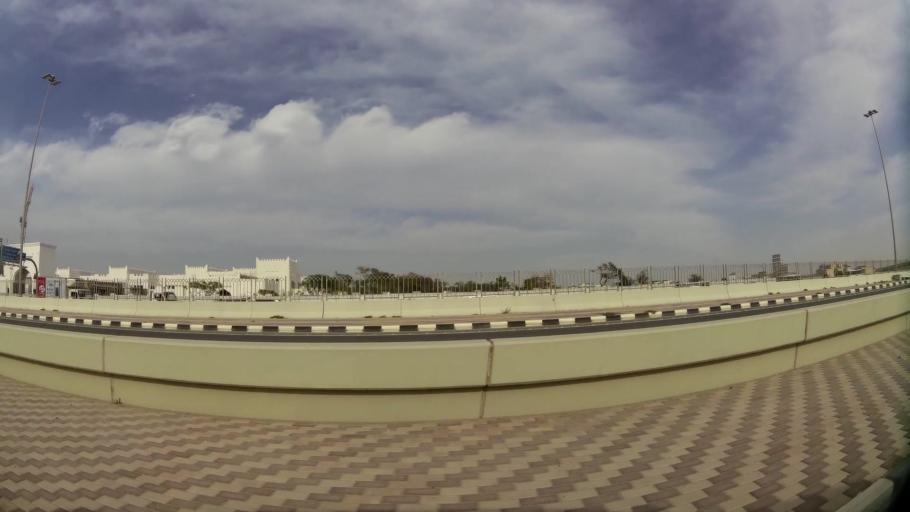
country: QA
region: Baladiyat ar Rayyan
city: Ar Rayyan
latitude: 25.2992
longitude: 51.4740
